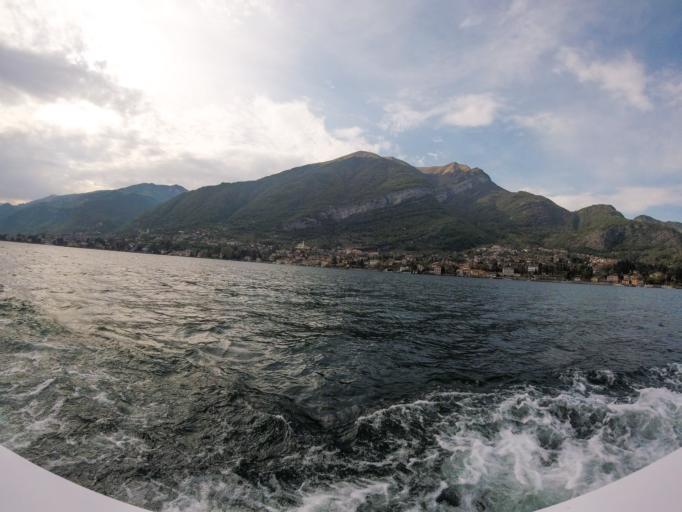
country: IT
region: Lombardy
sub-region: Provincia di Como
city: Tremezzo
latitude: 45.9760
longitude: 9.2172
